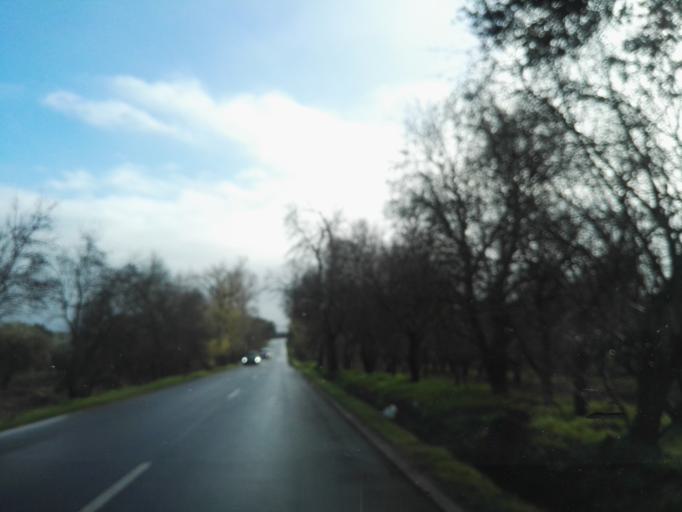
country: PT
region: Portalegre
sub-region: Elvas
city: Elvas
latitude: 38.9258
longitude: -7.1819
